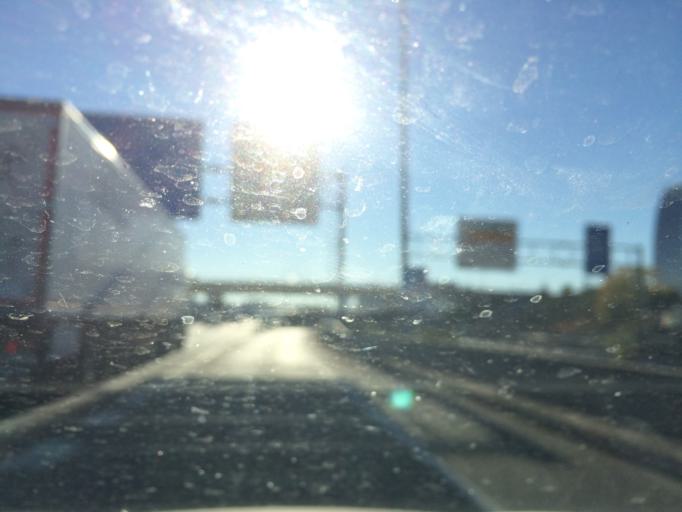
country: ES
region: Madrid
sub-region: Provincia de Madrid
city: Las Tablas
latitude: 40.5032
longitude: -3.6592
